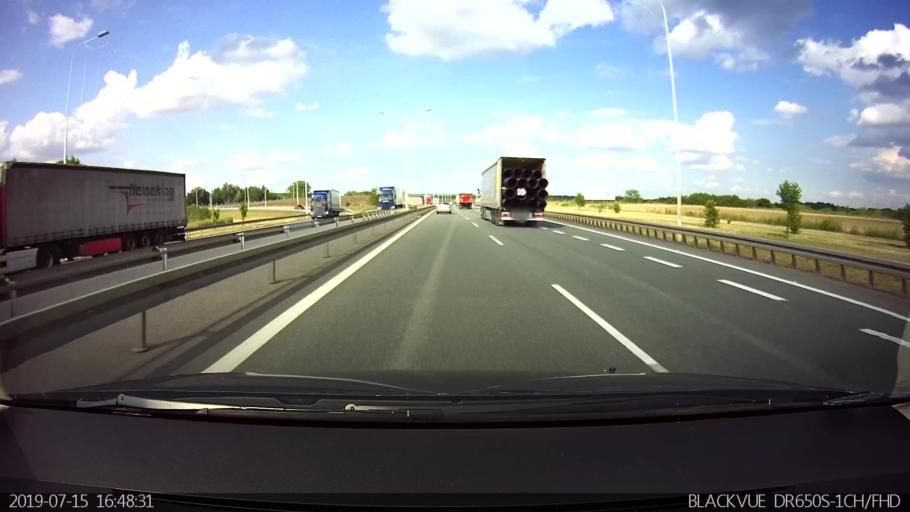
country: PL
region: Lower Silesian Voivodeship
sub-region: Powiat trzebnicki
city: Psary
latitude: 51.1740
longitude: 17.0830
